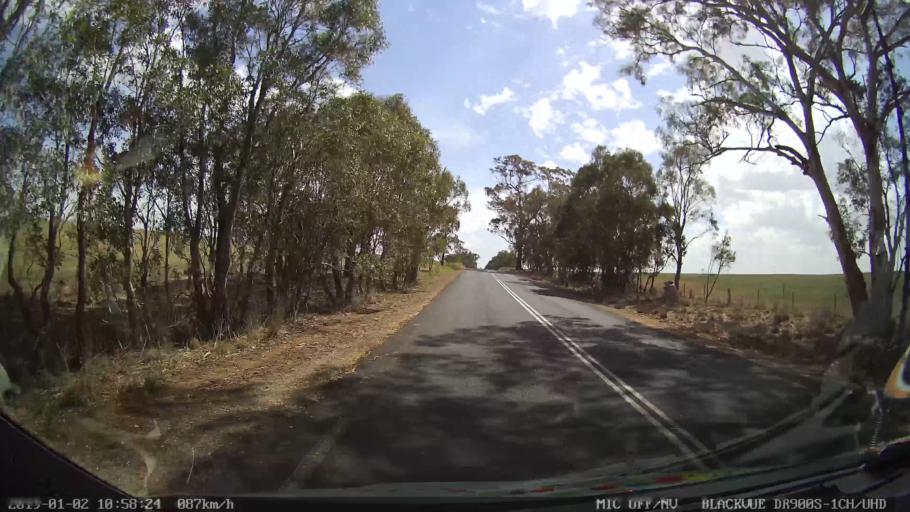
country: AU
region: New South Wales
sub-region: Cootamundra
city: Cootamundra
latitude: -34.6250
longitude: 148.2909
